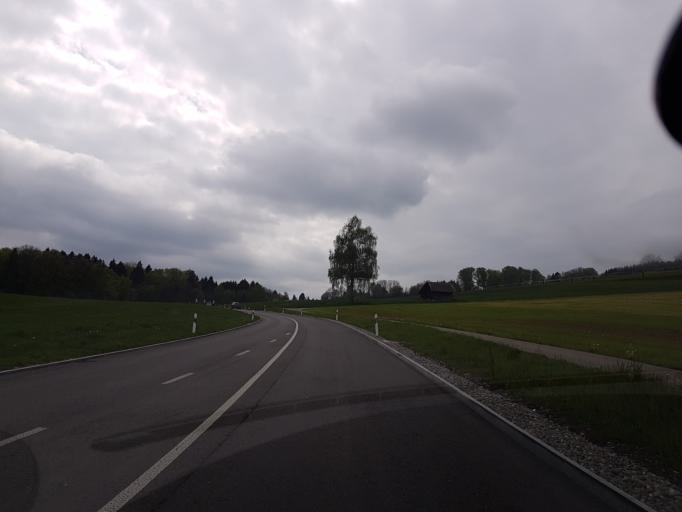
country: CH
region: Zurich
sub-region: Bezirk Dietikon
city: Birmensdorf
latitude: 47.3462
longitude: 8.4139
